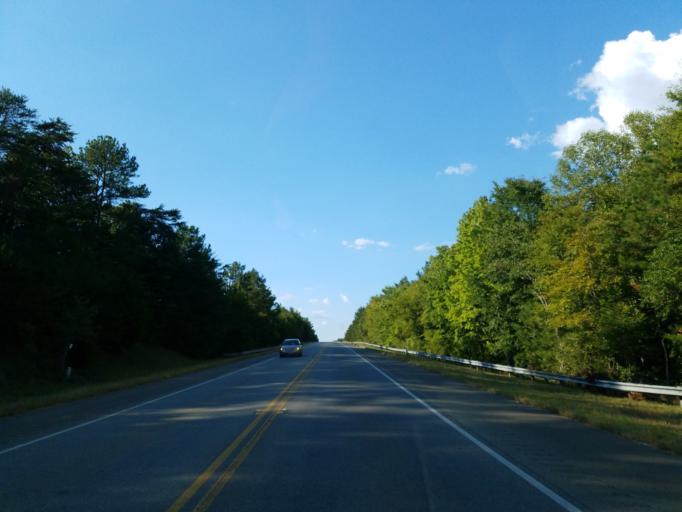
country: US
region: Georgia
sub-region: Murray County
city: Chatsworth
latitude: 34.6795
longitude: -84.7274
